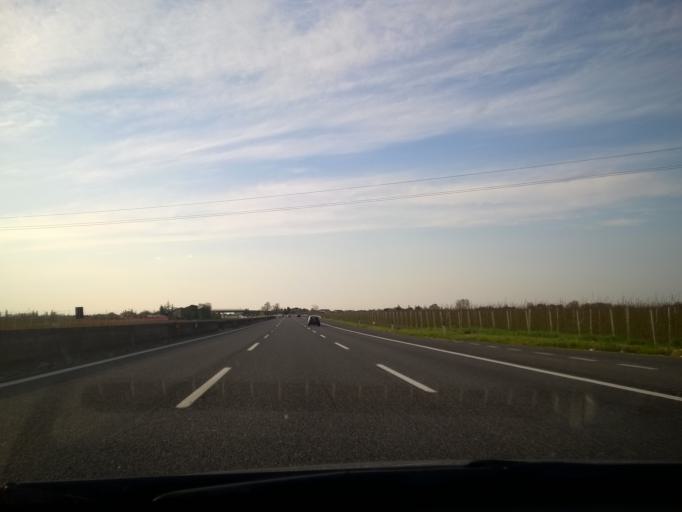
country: IT
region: Emilia-Romagna
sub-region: Forli-Cesena
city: Forlimpopoli
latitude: 44.2401
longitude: 12.1288
